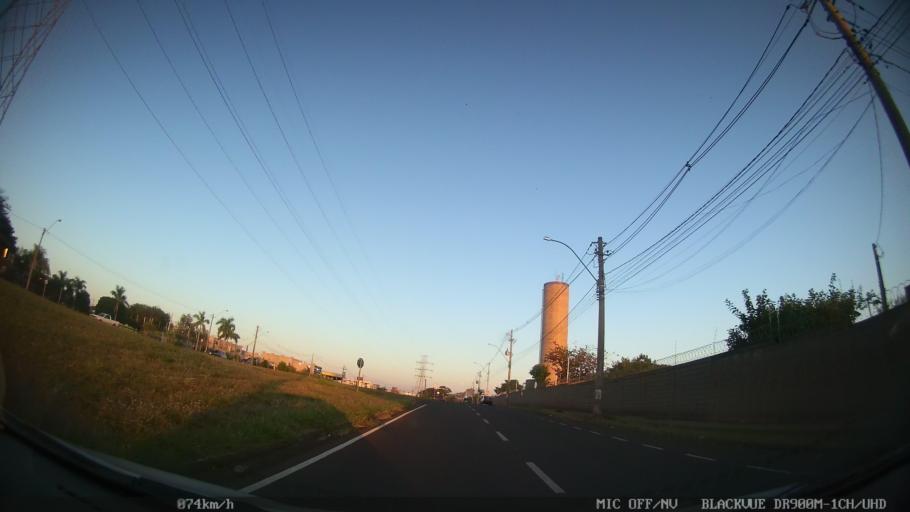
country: BR
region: Sao Paulo
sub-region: Sao Jose Do Rio Preto
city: Sao Jose do Rio Preto
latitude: -20.7792
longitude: -49.3438
